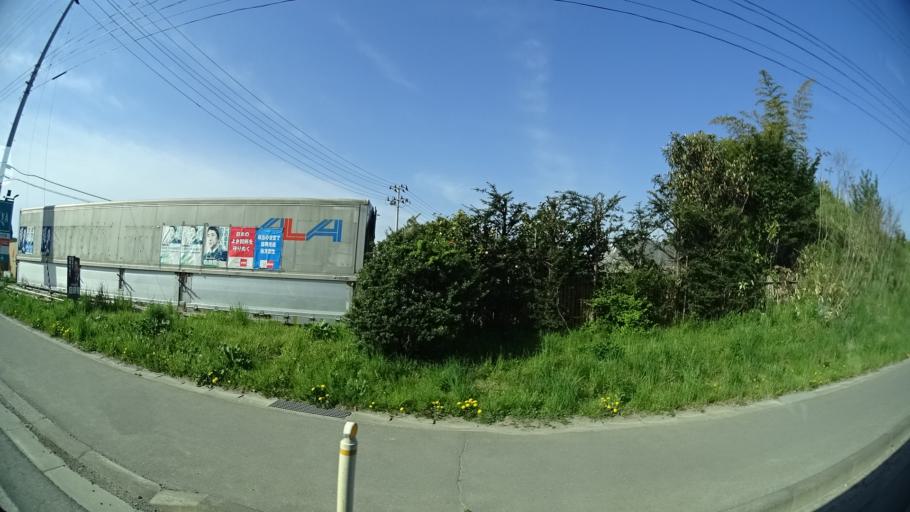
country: JP
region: Iwate
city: Ofunato
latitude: 39.0121
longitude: 141.6708
